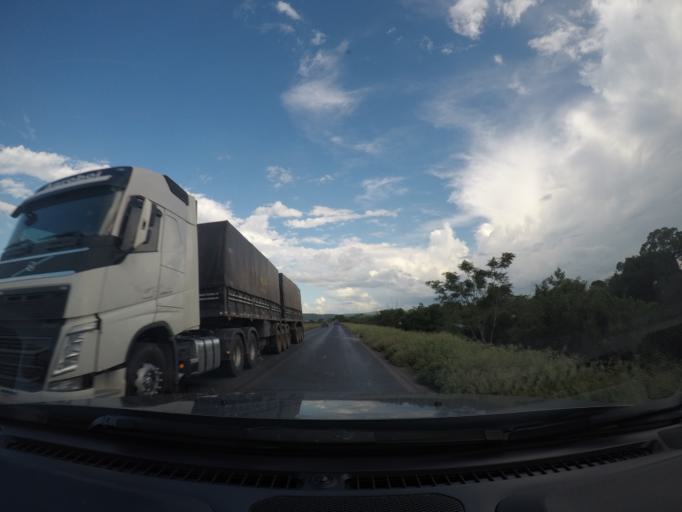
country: BR
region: Bahia
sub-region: Ibotirama
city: Ibotirama
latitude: -12.1813
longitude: -43.2364
